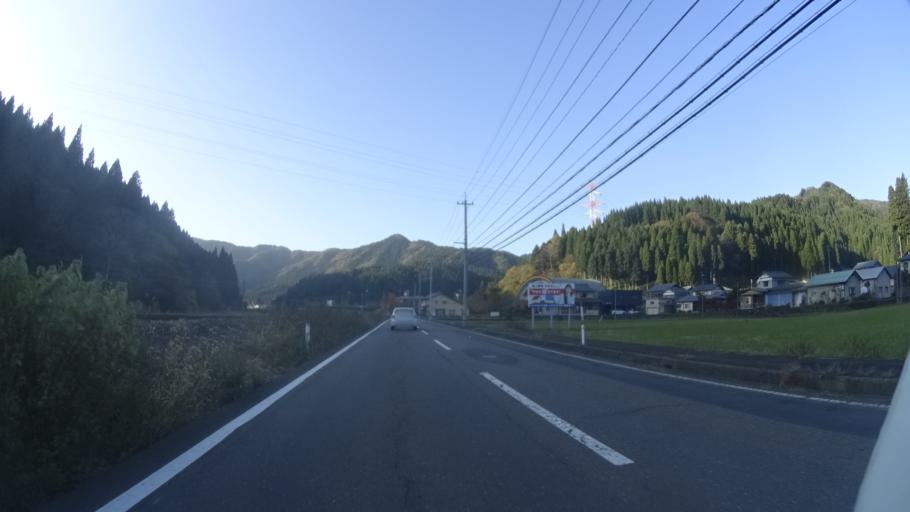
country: JP
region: Fukui
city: Ono
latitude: 36.0030
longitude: 136.4041
